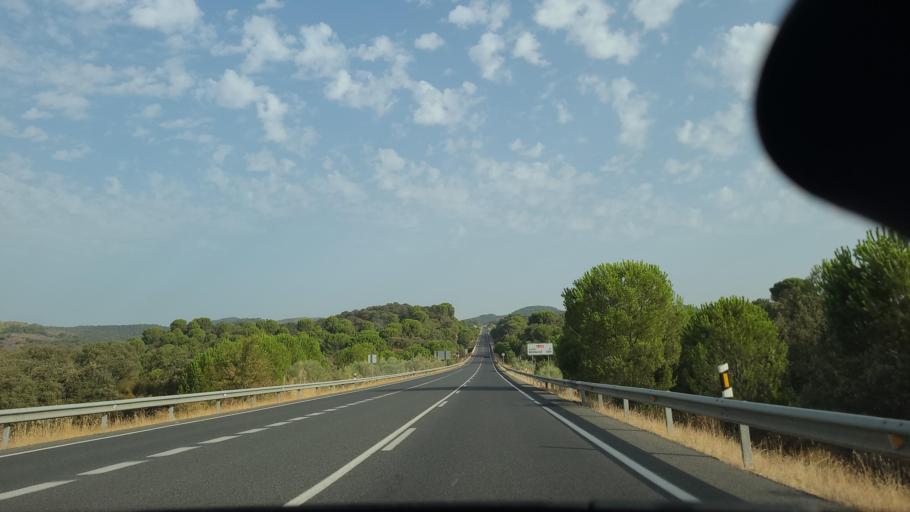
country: ES
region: Andalusia
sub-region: Province of Cordoba
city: Cordoba
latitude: 38.0013
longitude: -4.7988
